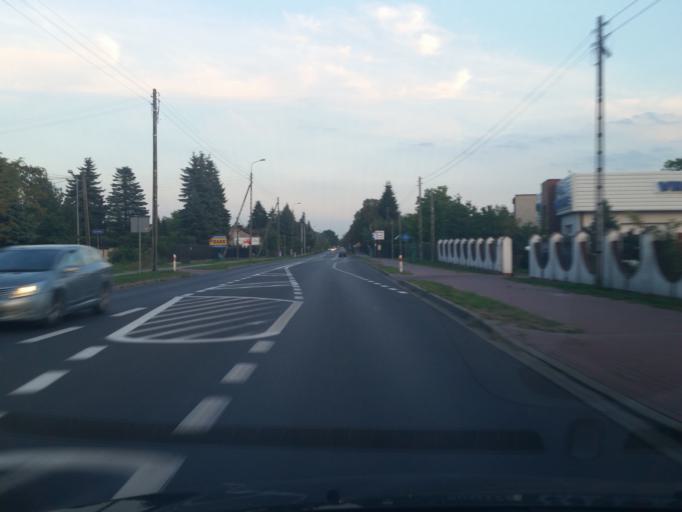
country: PL
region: Masovian Voivodeship
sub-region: Powiat legionowski
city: Jablonna
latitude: 52.3818
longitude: 20.9074
